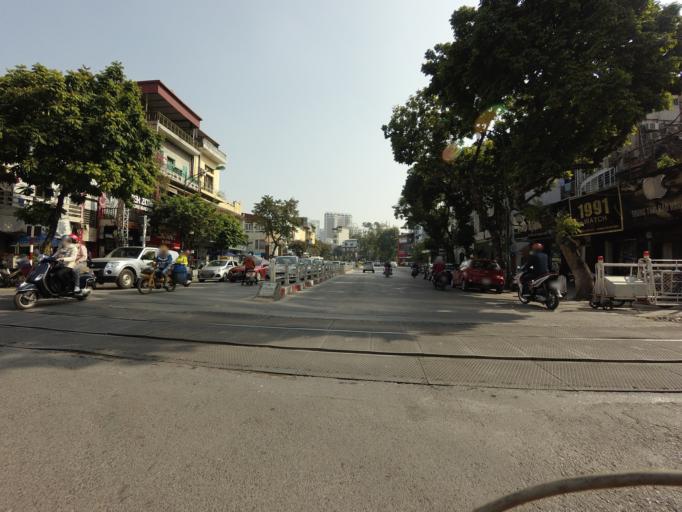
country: VN
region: Ha Noi
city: Hanoi
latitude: 21.0291
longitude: 105.8426
